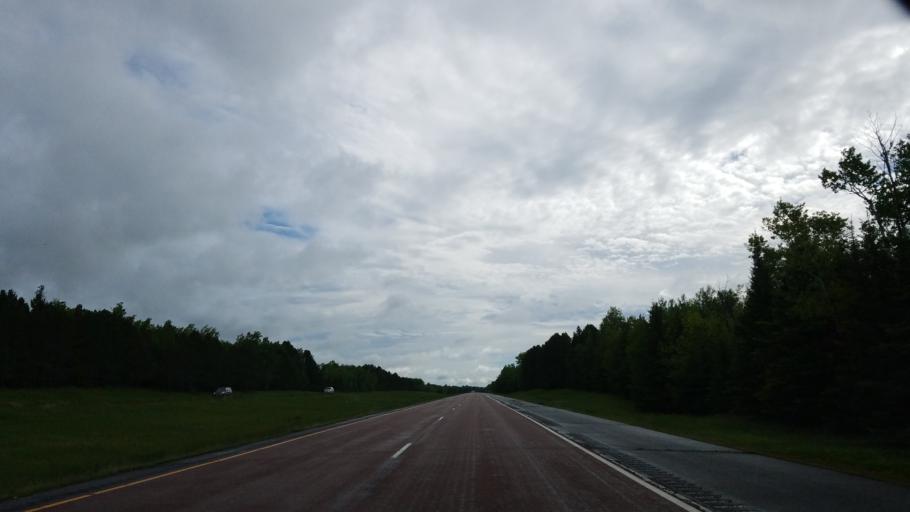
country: US
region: Minnesota
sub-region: Lake County
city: Two Harbors
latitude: 46.9186
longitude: -91.8693
